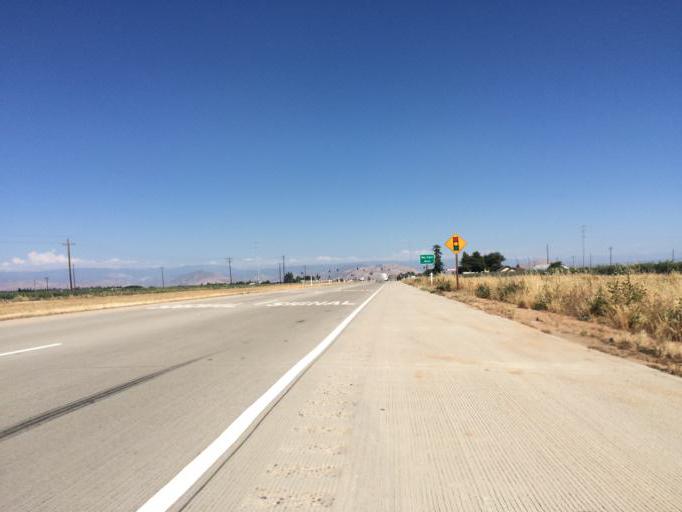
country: US
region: California
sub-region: Fresno County
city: Sanger
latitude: 36.7357
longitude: -119.6141
